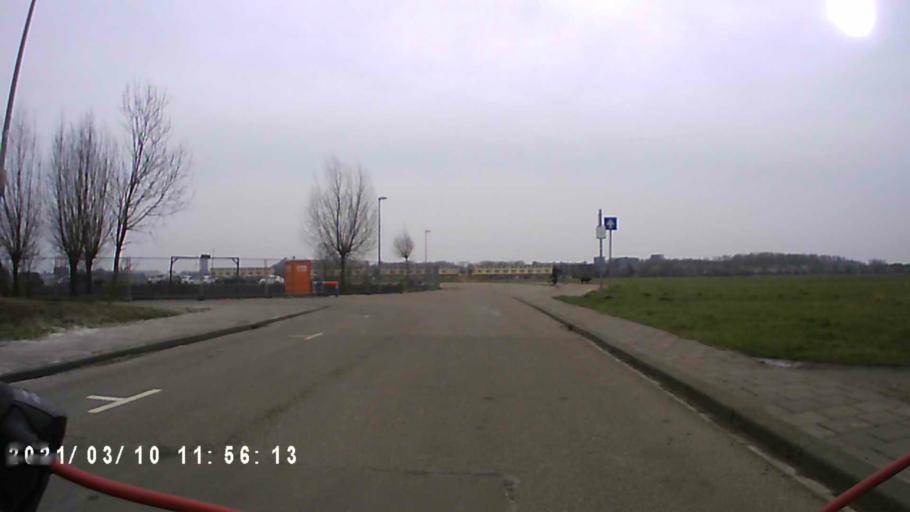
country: NL
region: Groningen
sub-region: Gemeente Zuidhorn
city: Aduard
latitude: 53.2294
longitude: 6.5043
